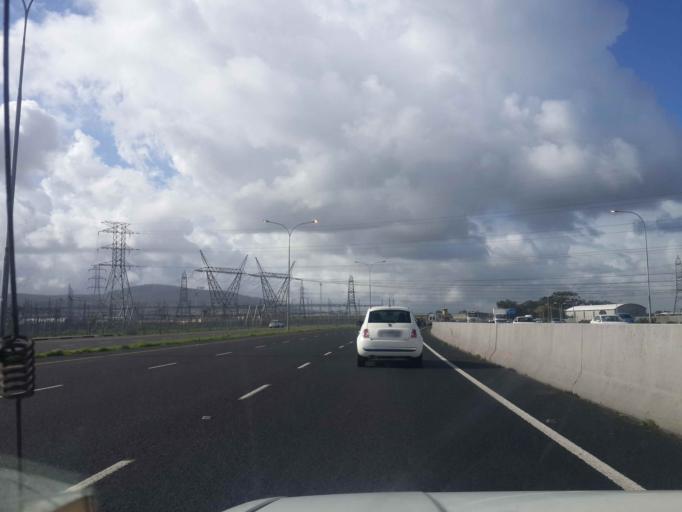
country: ZA
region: Western Cape
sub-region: City of Cape Town
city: Sunset Beach
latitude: -33.8853
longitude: 18.5334
